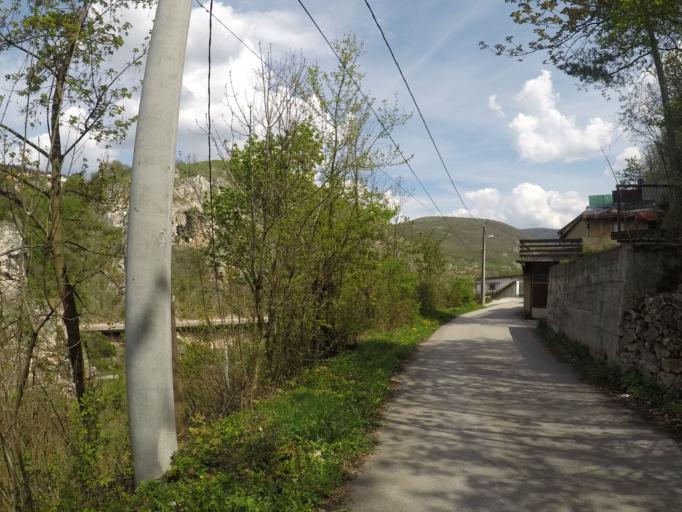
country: BA
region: Federation of Bosnia and Herzegovina
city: Kobilja Glava
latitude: 43.8575
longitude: 18.4412
